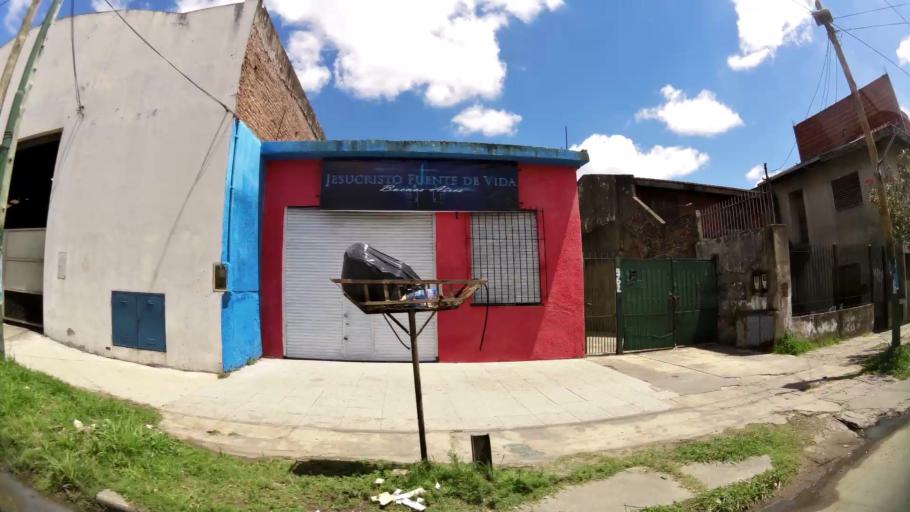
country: AR
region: Buenos Aires
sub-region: Partido de Lanus
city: Lanus
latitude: -34.7240
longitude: -58.4268
